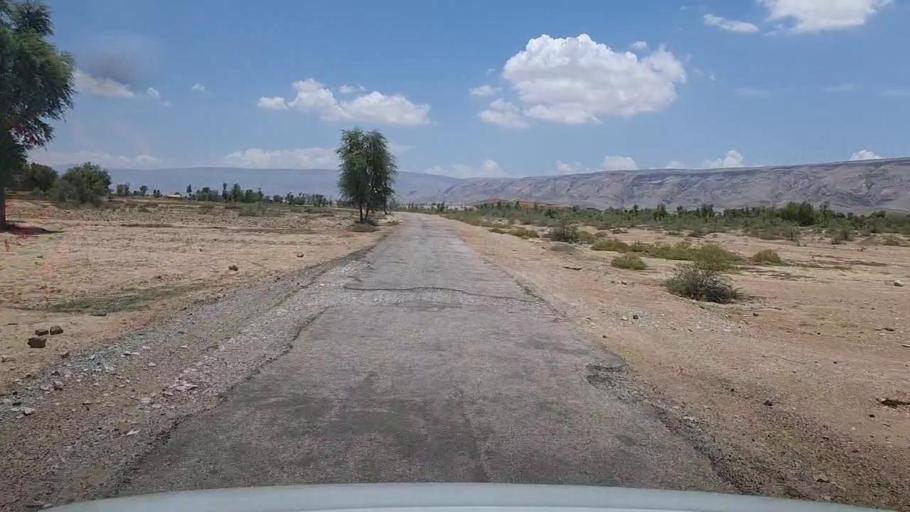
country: PK
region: Sindh
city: Bhan
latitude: 26.2710
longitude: 67.5228
